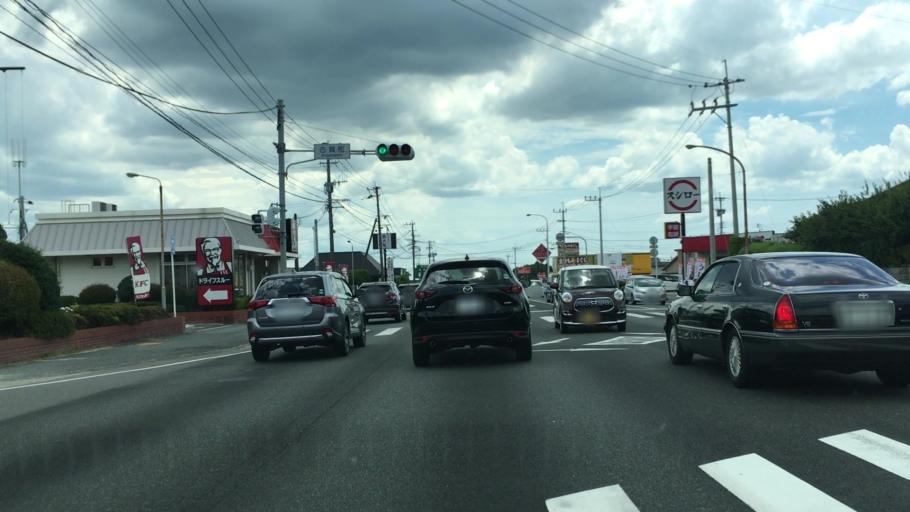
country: JP
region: Saga Prefecture
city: Tosu
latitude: 33.3876
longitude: 130.4998
